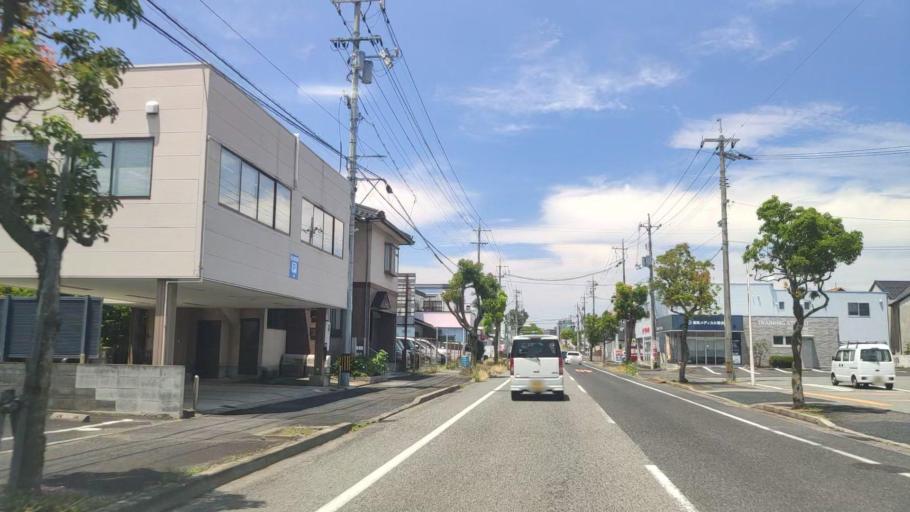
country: JP
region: Tottori
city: Tottori
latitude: 35.4807
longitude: 134.2350
